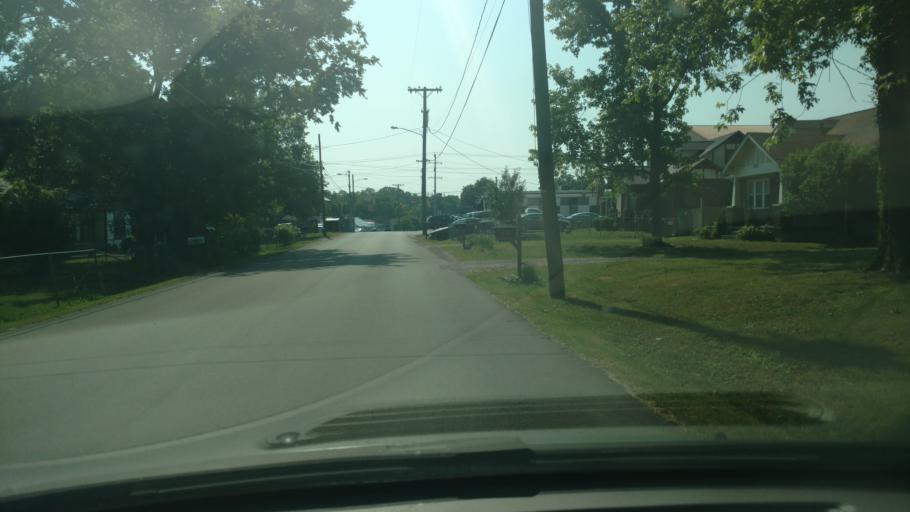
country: US
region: Tennessee
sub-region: Davidson County
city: Nashville
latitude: 36.2199
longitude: -86.7289
